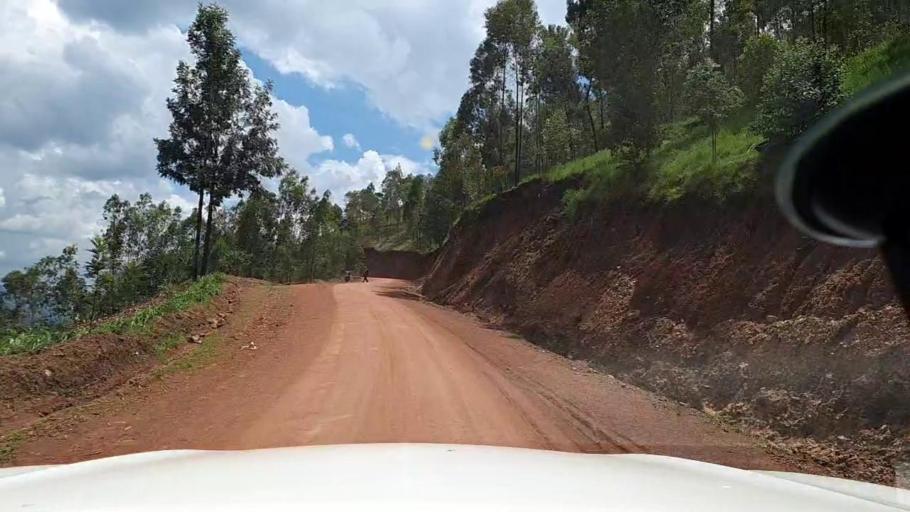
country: RW
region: Northern Province
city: Byumba
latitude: -1.7521
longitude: 29.8445
